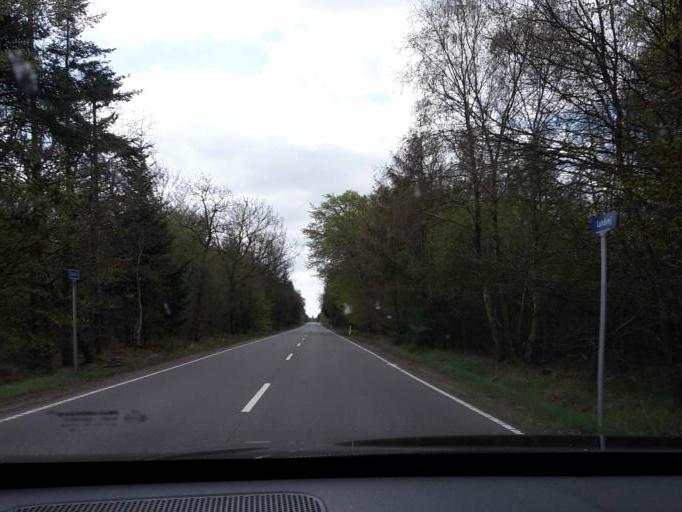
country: DK
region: South Denmark
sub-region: Varde Kommune
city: Olgod
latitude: 55.6991
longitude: 8.6064
